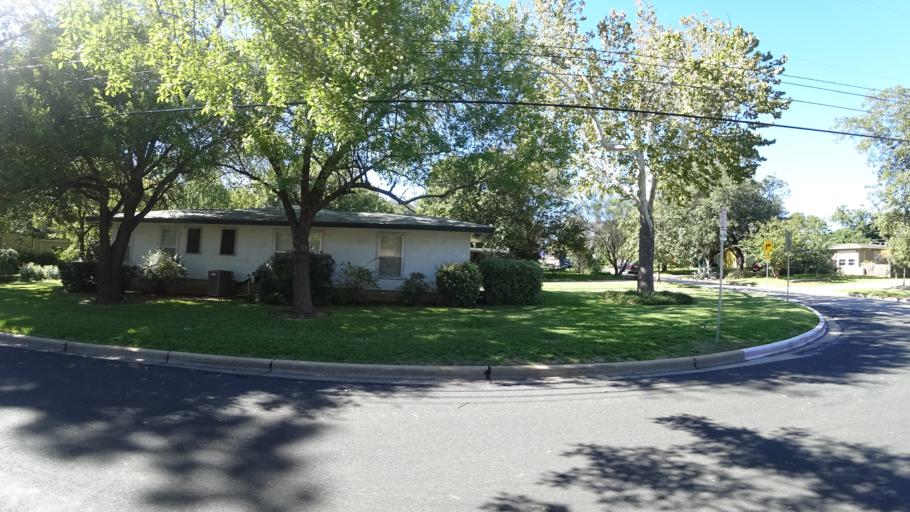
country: US
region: Texas
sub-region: Travis County
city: Austin
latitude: 30.3327
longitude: -97.7382
